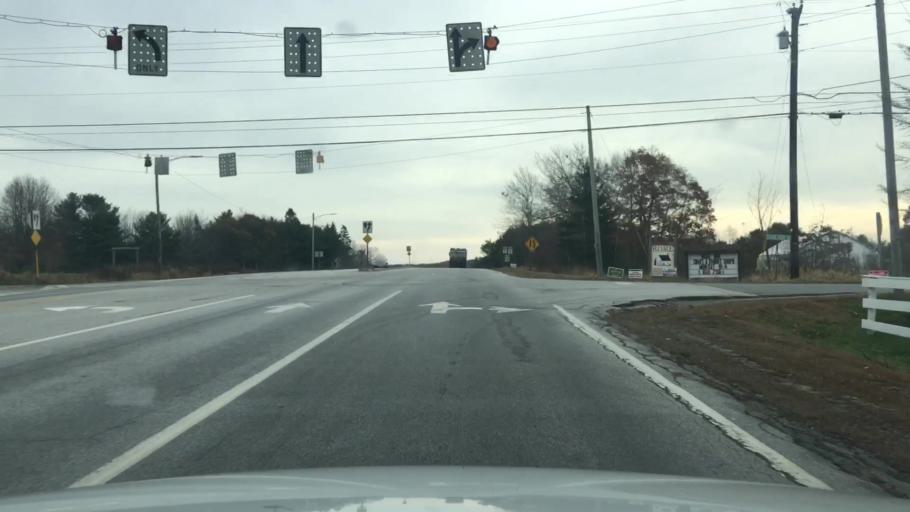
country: US
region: Maine
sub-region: Hancock County
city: Orland
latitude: 44.5738
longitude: -68.7314
